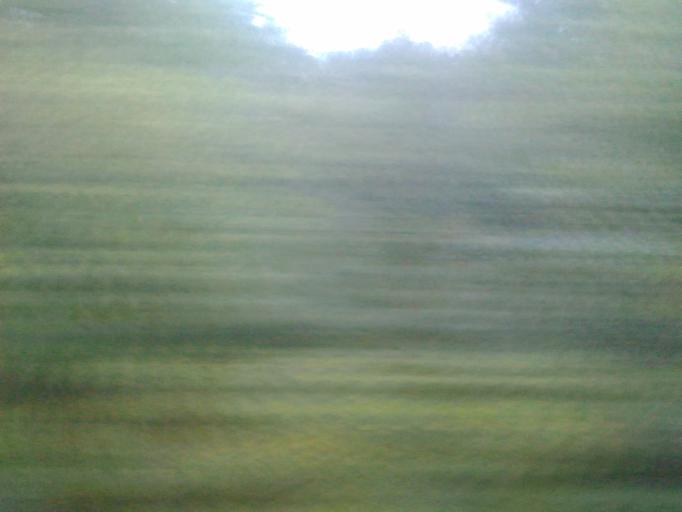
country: RU
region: Ulyanovsk
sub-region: Ulyanovskiy Rayon
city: Ulyanovsk
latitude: 54.3022
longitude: 48.3226
